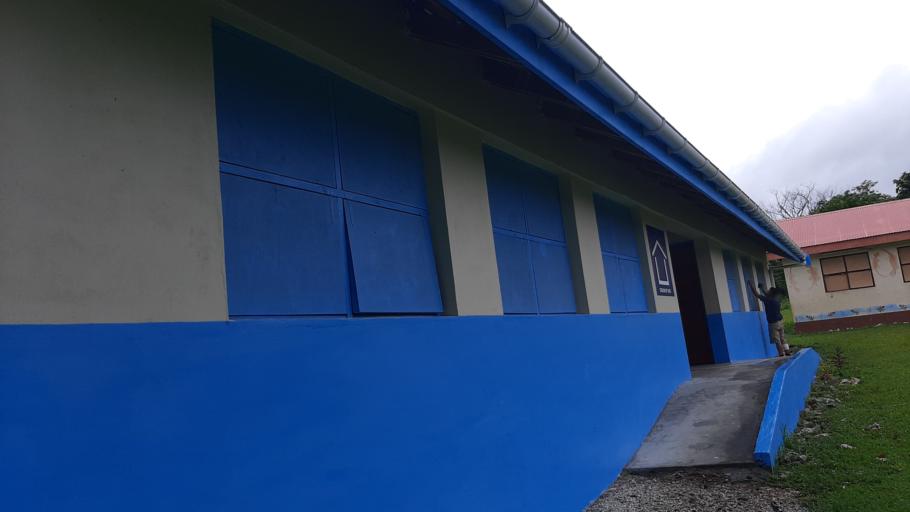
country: VU
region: Malampa
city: Lakatoro
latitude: -16.6691
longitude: 168.1300
